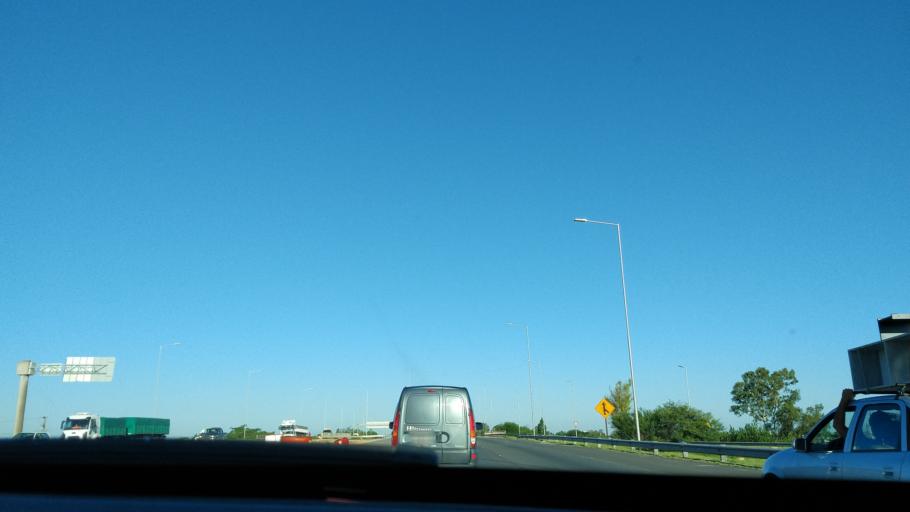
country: AR
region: Cordoba
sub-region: Departamento de Capital
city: Cordoba
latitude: -31.3552
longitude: -64.1873
